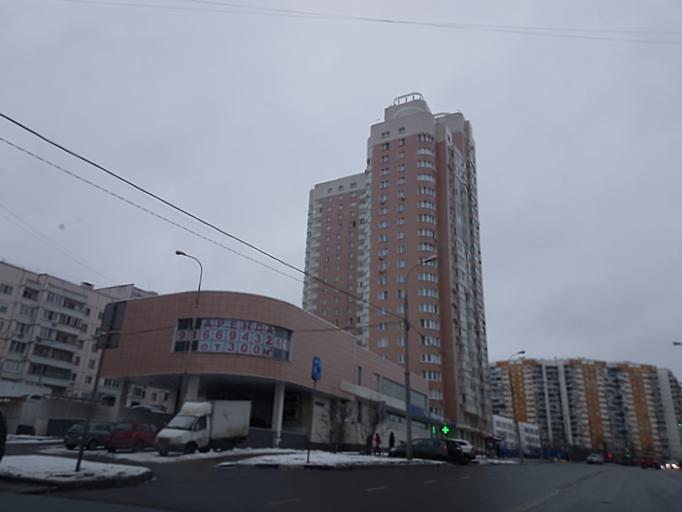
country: RU
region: Moskovskaya
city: Pavshino
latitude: 55.8302
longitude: 37.3543
